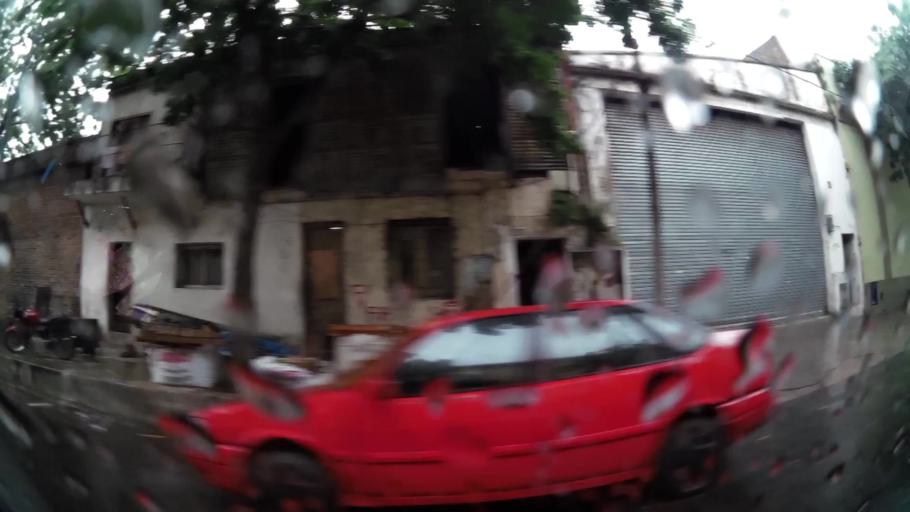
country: AR
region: Buenos Aires
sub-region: Partido de Avellaneda
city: Avellaneda
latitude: -34.6466
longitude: -58.3652
